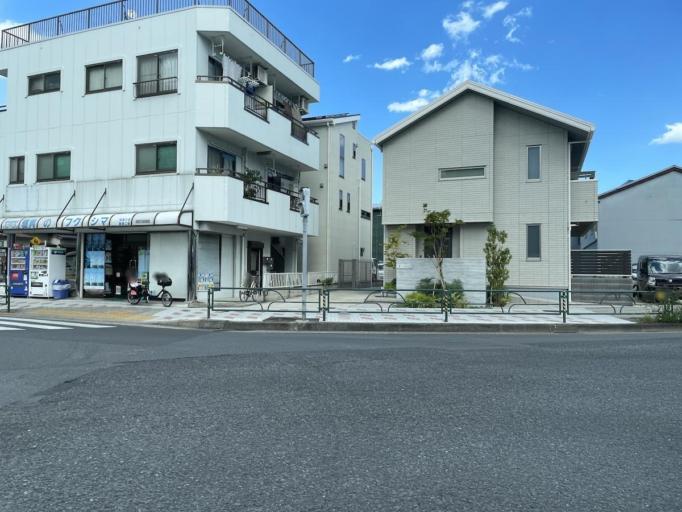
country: JP
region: Tokyo
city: Urayasu
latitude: 35.7230
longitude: 139.8312
